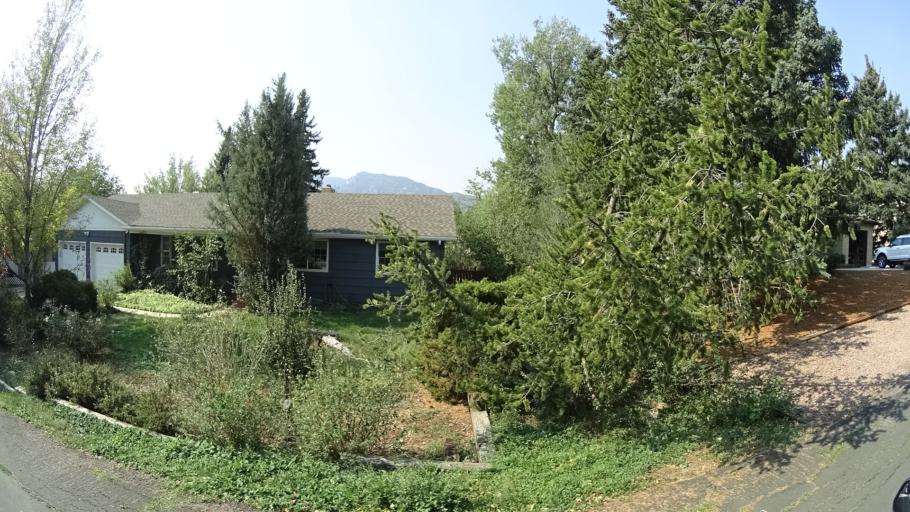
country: US
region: Colorado
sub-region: El Paso County
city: Colorado Springs
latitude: 38.8113
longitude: -104.8334
